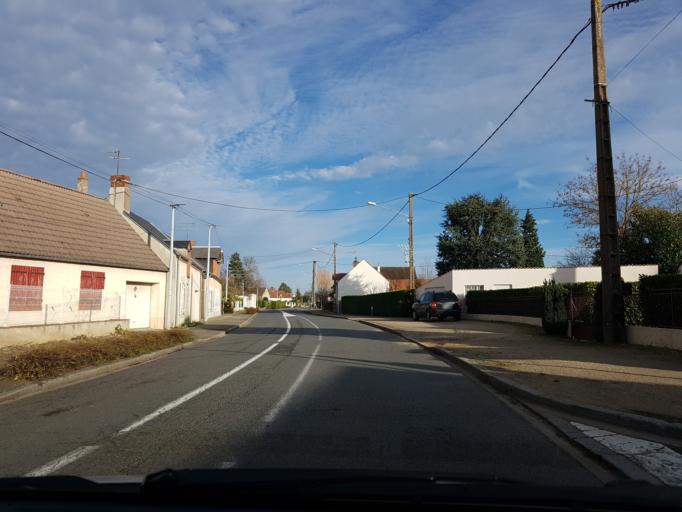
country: FR
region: Centre
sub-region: Departement du Loiret
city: Darvoy
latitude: 47.8575
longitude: 2.1000
